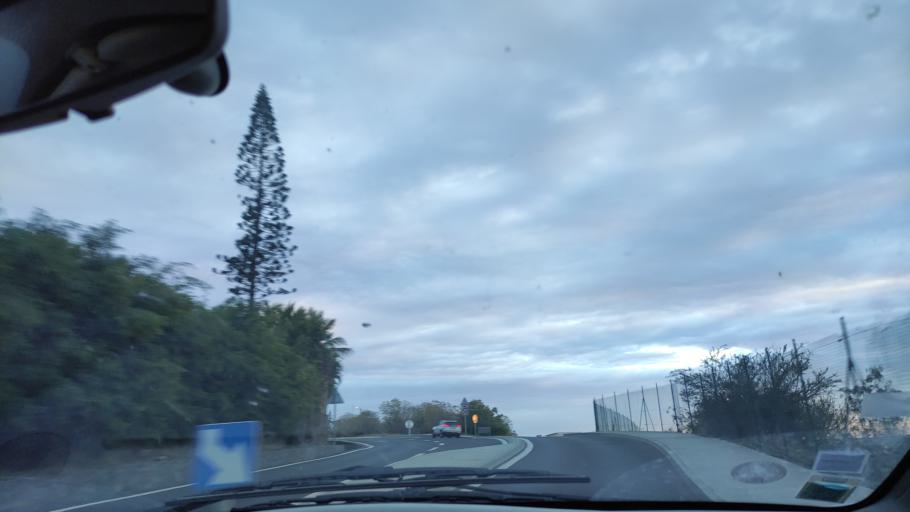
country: RE
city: Piton Saint-Leu
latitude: -21.2062
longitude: 55.2967
